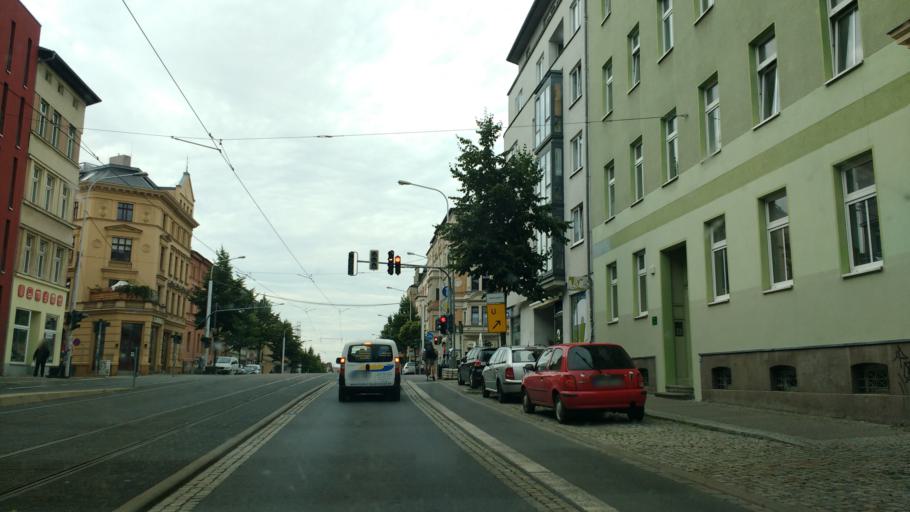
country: DE
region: Saxony-Anhalt
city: Halle (Saale)
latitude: 51.4907
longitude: 11.9761
